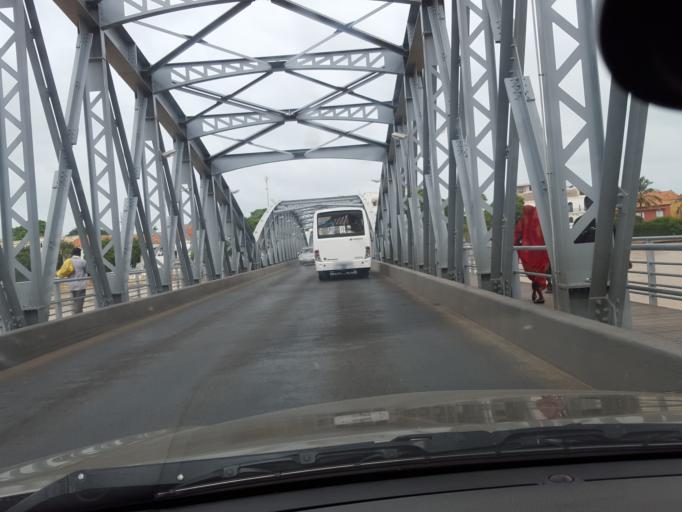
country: SN
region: Saint-Louis
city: Saint-Louis
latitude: 16.0259
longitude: -16.5019
